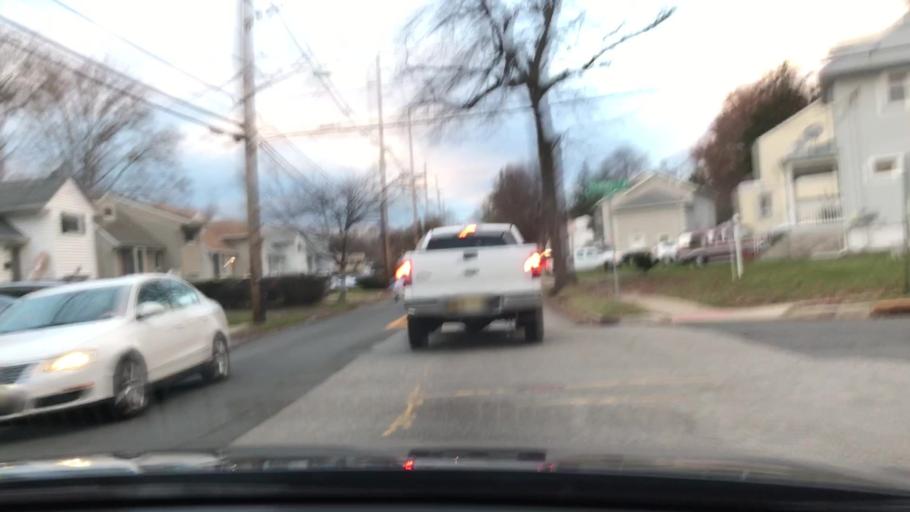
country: US
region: New Jersey
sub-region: Bergen County
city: Maywood
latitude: 40.8922
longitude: -74.0671
